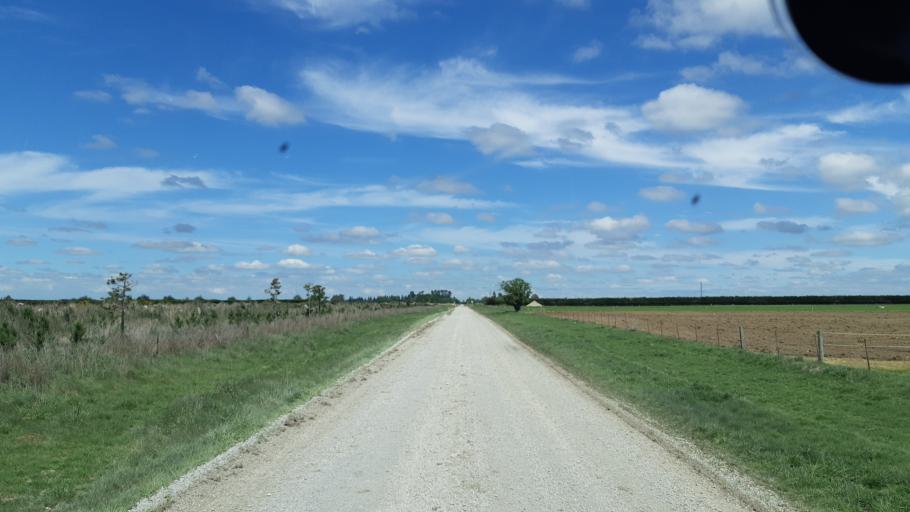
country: NZ
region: Canterbury
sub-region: Ashburton District
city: Methven
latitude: -43.7146
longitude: 171.4582
